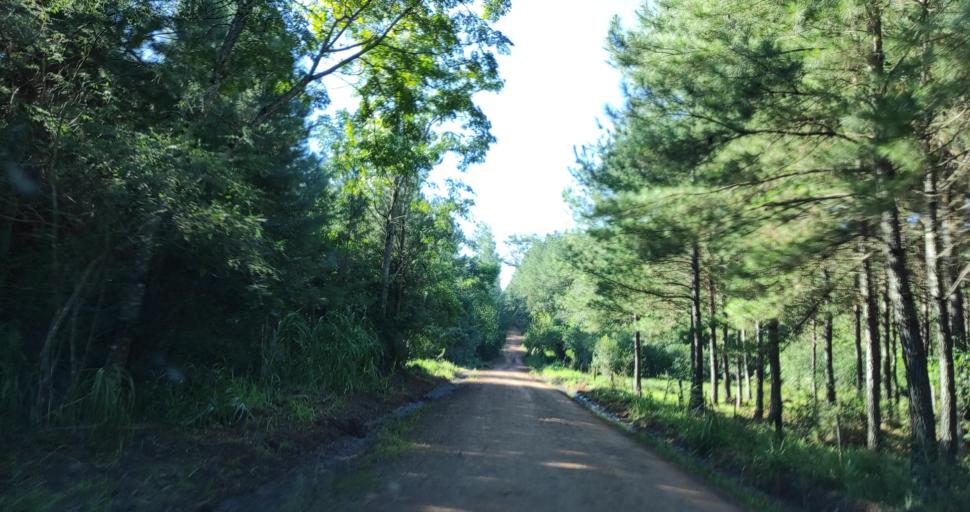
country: AR
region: Misiones
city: Capiovi
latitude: -26.9287
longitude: -55.0010
